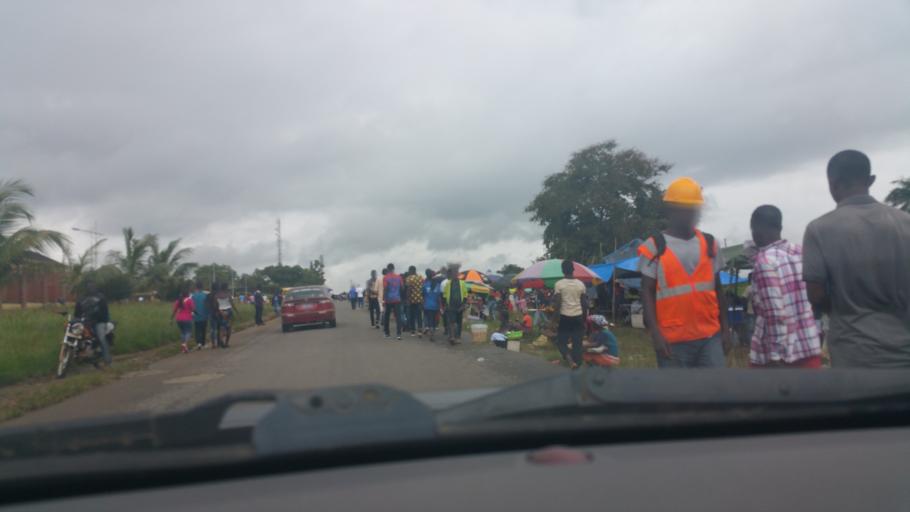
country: LR
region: Montserrado
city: Bensonville City
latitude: 6.3760
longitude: -10.6182
